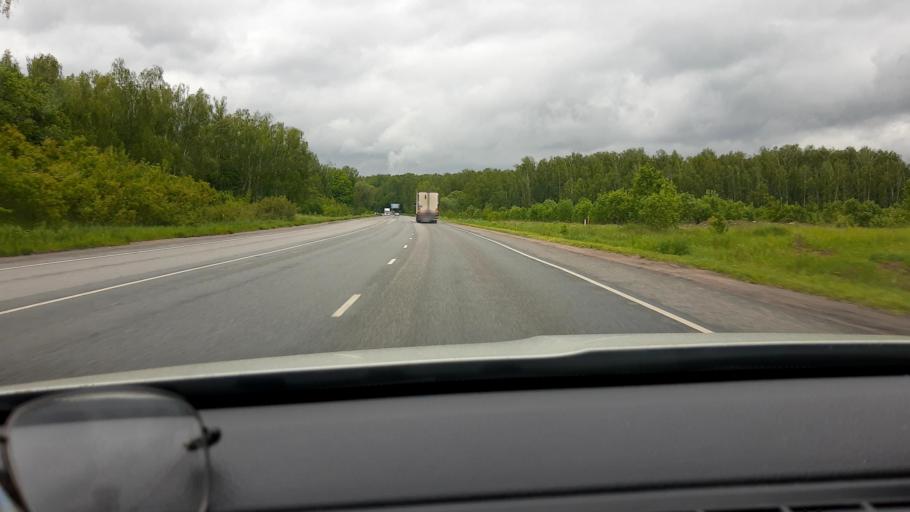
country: RU
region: Moskovskaya
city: Gorki-Leninskiye
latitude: 55.5243
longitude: 37.7899
